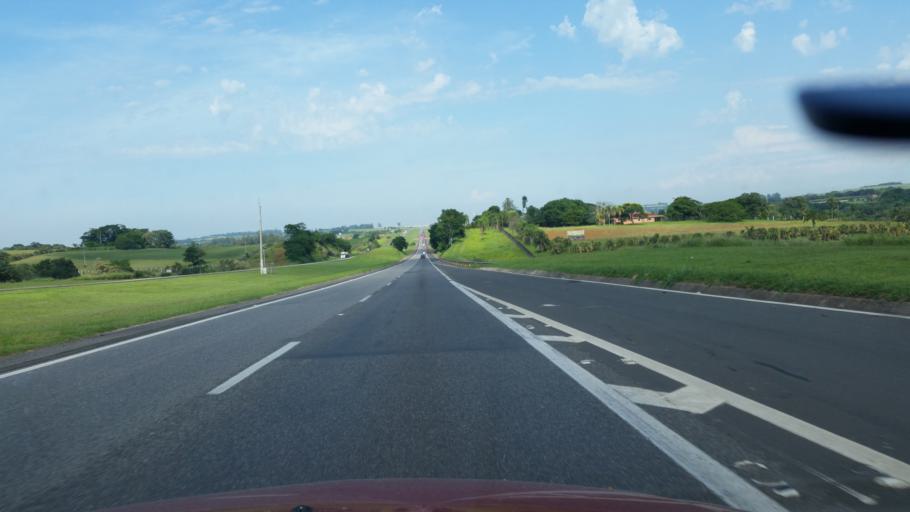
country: BR
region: Sao Paulo
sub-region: Tatui
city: Tatui
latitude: -23.2588
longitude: -47.8627
